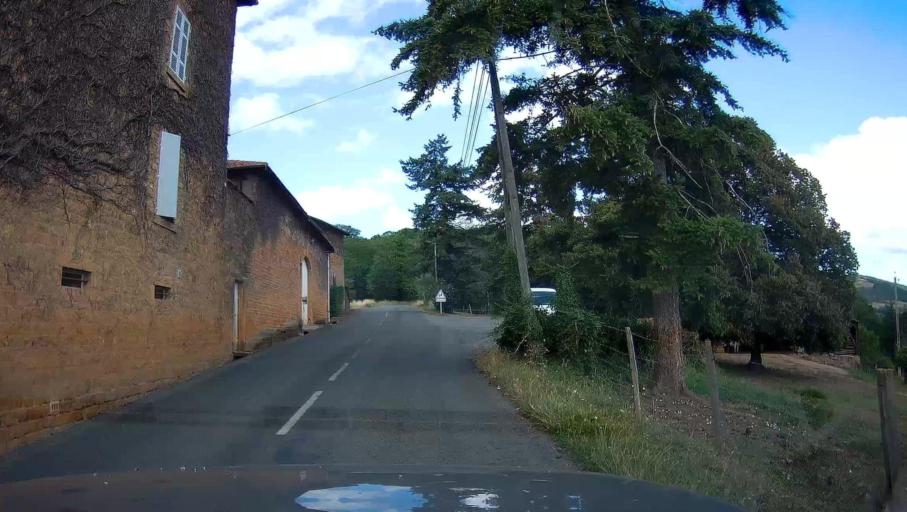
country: FR
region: Rhone-Alpes
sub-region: Departement du Rhone
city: Cogny
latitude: 45.9777
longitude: 4.5989
